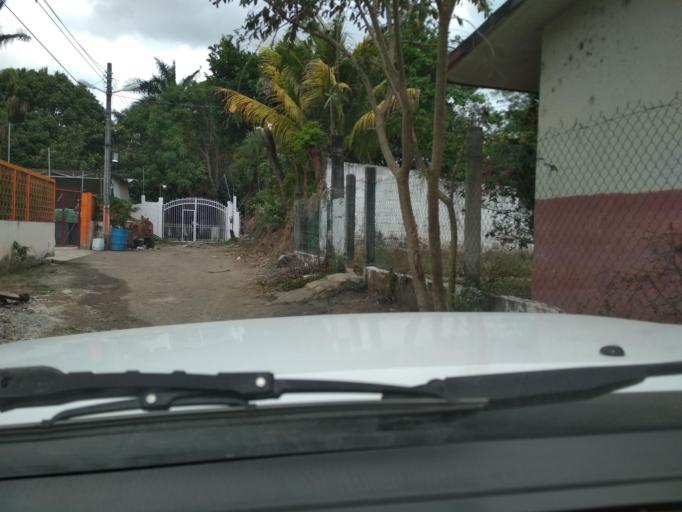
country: MX
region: Veracruz
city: Paso del Toro
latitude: 19.0537
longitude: -96.1361
